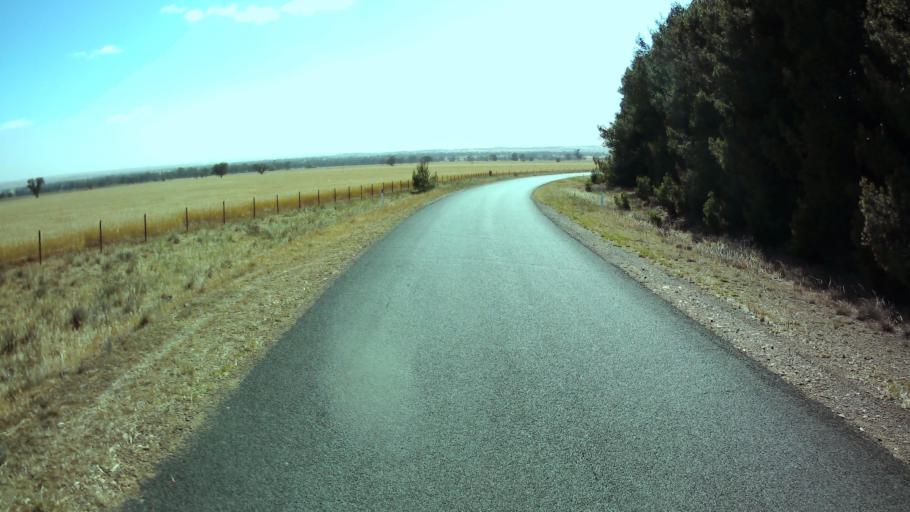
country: AU
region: New South Wales
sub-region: Weddin
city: Grenfell
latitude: -34.0617
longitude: 148.2679
